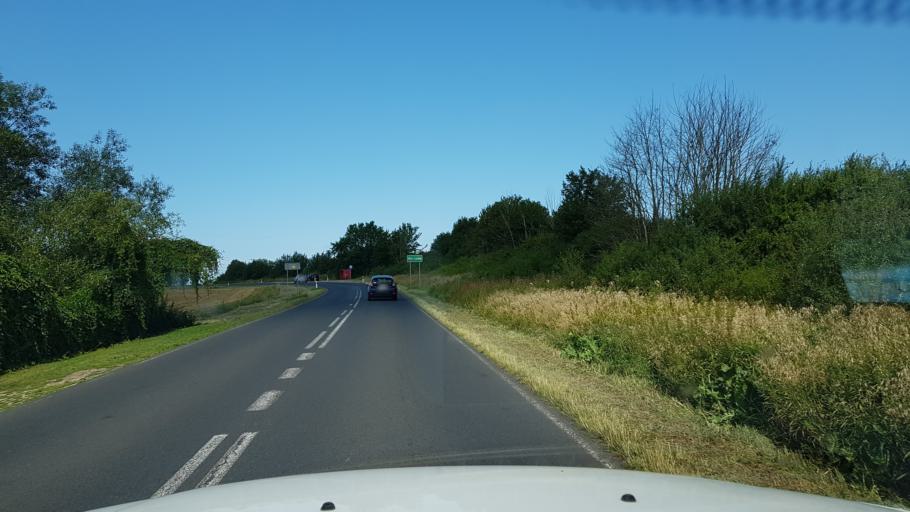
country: PL
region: West Pomeranian Voivodeship
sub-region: Powiat gryficki
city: Trzebiatow
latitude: 54.0783
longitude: 15.2195
